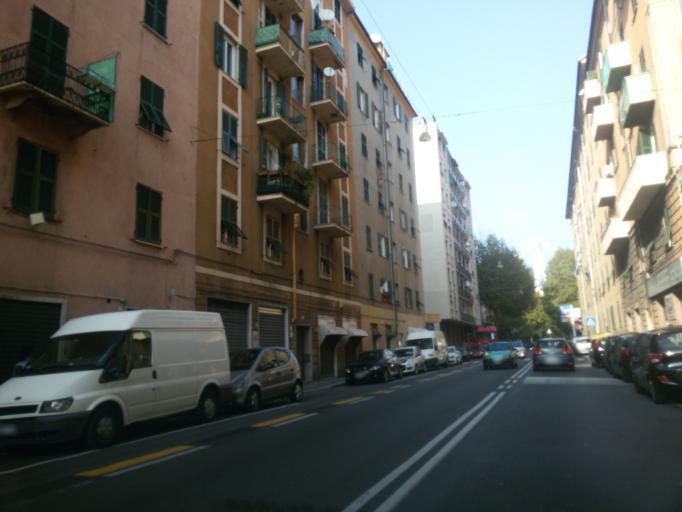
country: IT
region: Liguria
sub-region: Provincia di Genova
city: San Teodoro
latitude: 44.4209
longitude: 8.8879
